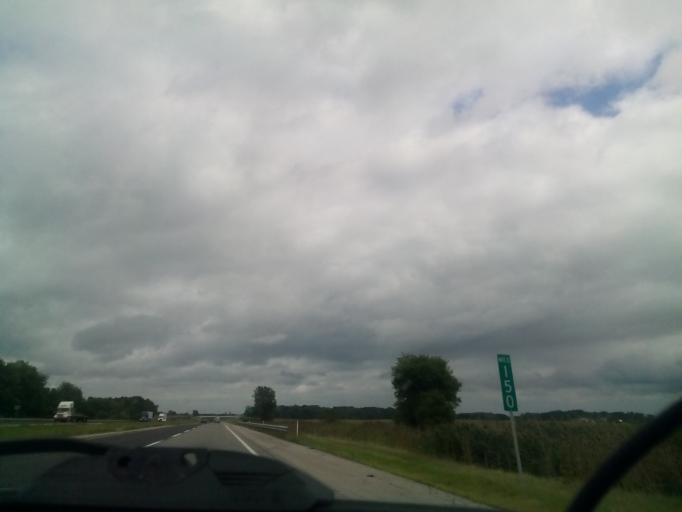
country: US
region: Indiana
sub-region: Steuben County
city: Fremont
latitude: 41.6912
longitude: -84.9001
